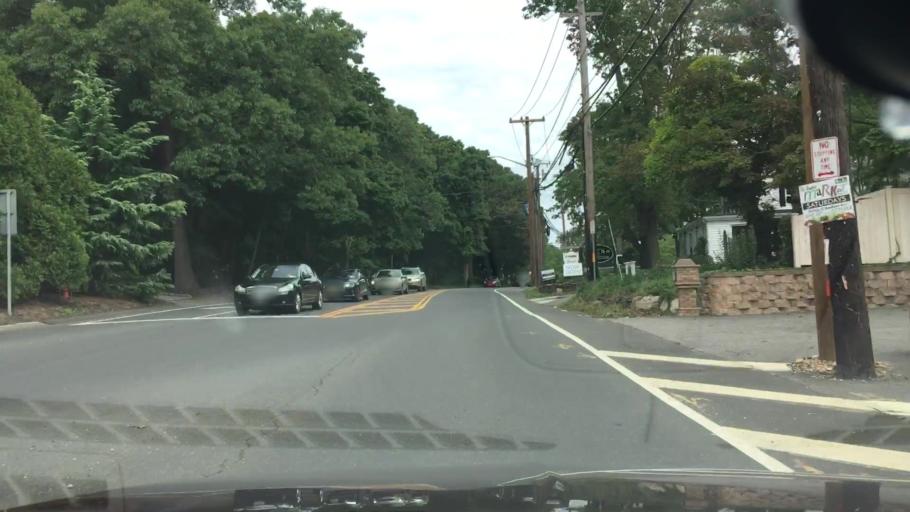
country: US
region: New York
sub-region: Suffolk County
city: Saint James
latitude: 40.8747
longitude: -73.1707
